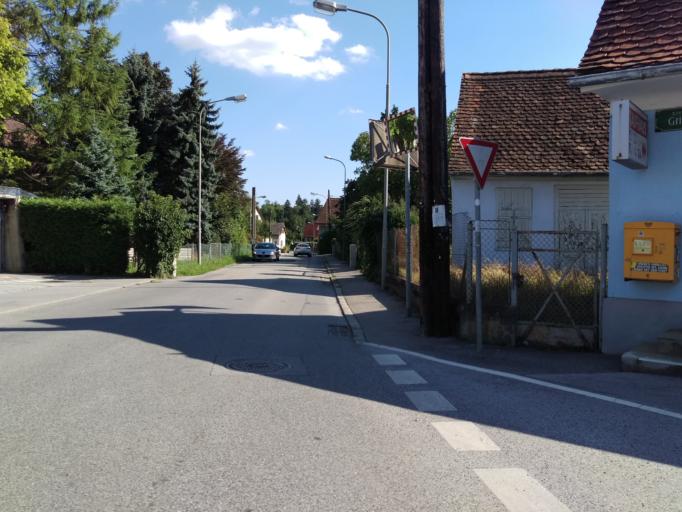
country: AT
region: Styria
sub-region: Graz Stadt
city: Wetzelsdorf
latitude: 47.0644
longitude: 15.3874
